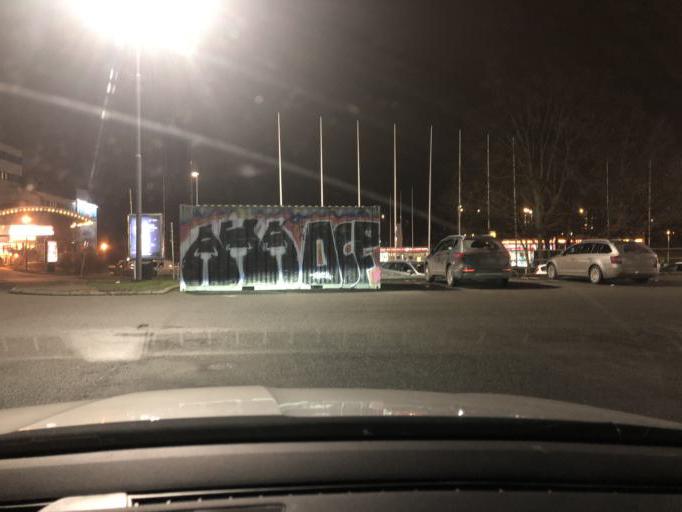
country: SE
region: Stockholm
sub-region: Botkyrka Kommun
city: Fittja
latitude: 59.2542
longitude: 17.8549
